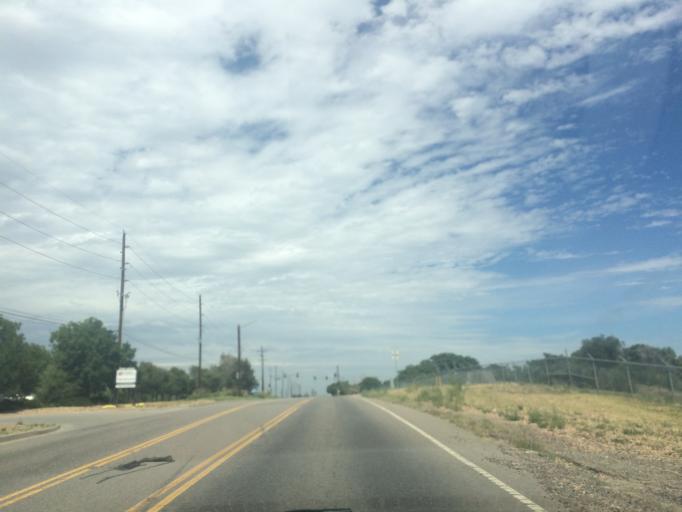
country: US
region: Colorado
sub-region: Adams County
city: Welby
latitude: 39.8147
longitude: -104.9592
